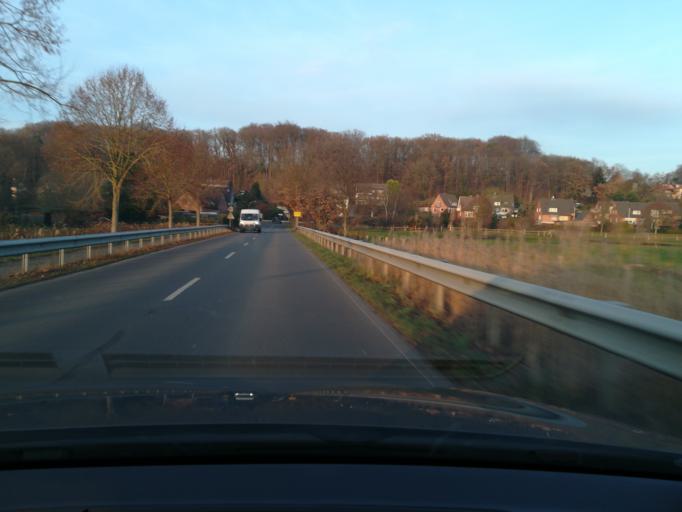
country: DE
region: Schleswig-Holstein
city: Escheburg
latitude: 53.4599
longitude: 10.3180
